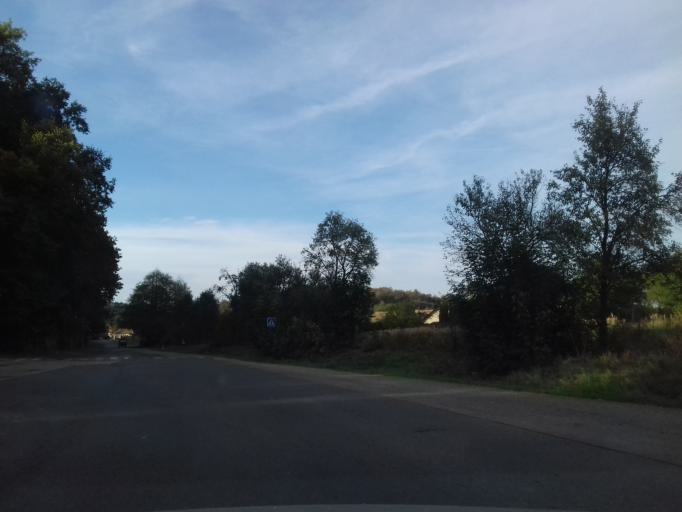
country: CZ
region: Central Bohemia
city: Neveklov
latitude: 49.7562
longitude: 14.5297
